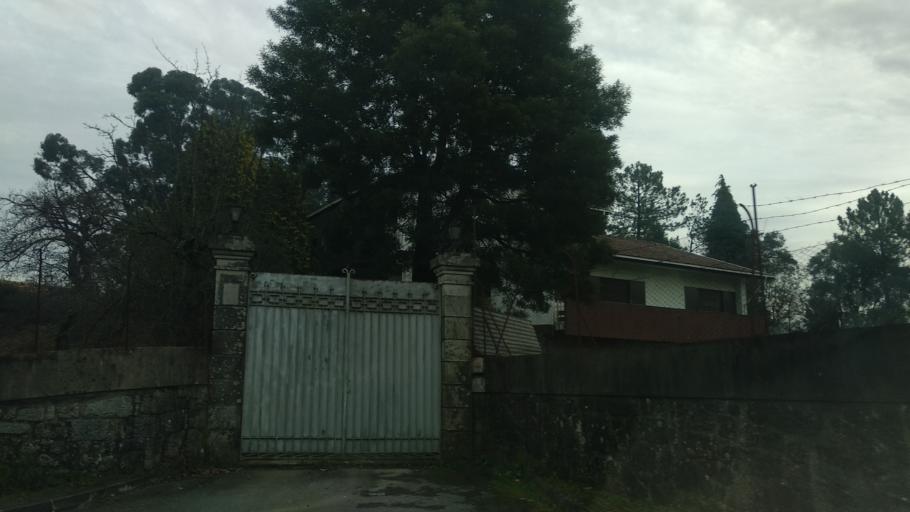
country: PT
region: Braga
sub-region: Braga
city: Braga
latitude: 41.5269
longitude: -8.4436
